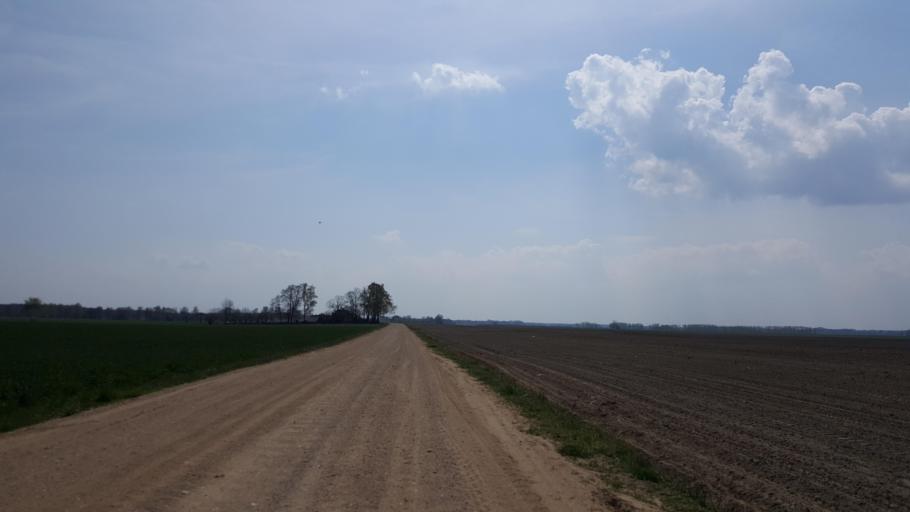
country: BY
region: Brest
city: Kamyanyets
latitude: 52.2993
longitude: 23.9093
